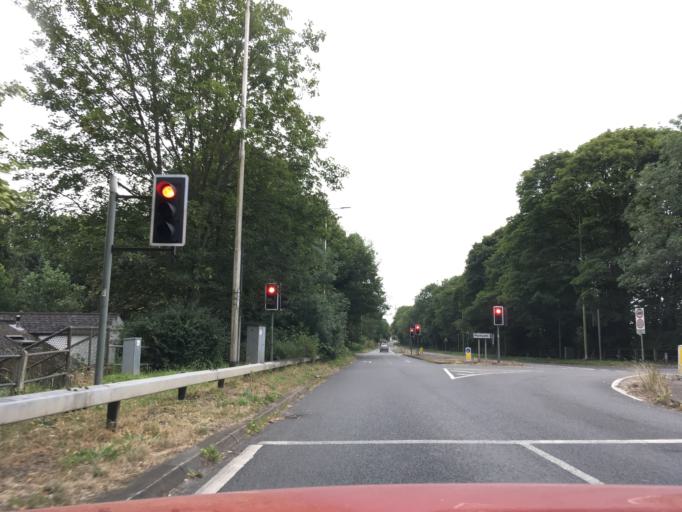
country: GB
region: England
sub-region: Hertfordshire
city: Markyate
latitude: 51.8397
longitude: -0.4638
